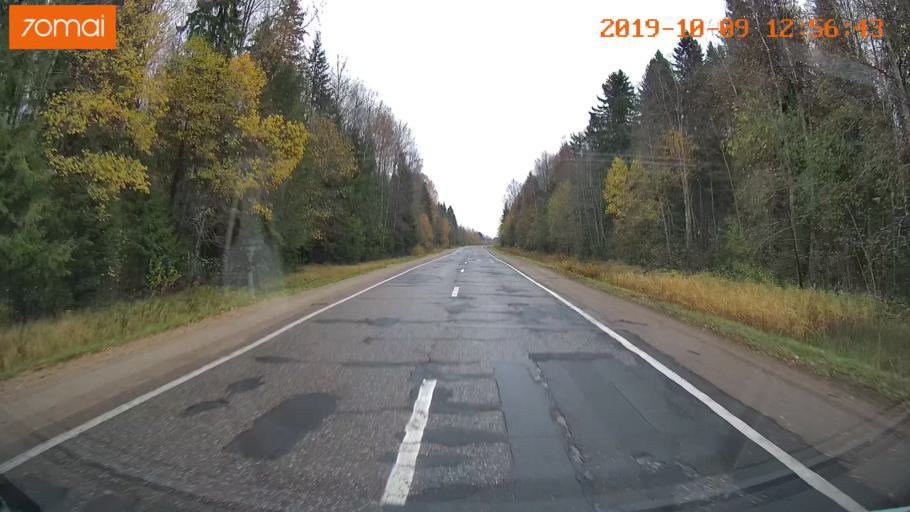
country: RU
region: Jaroslavl
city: Prechistoye
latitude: 58.3942
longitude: 40.4212
